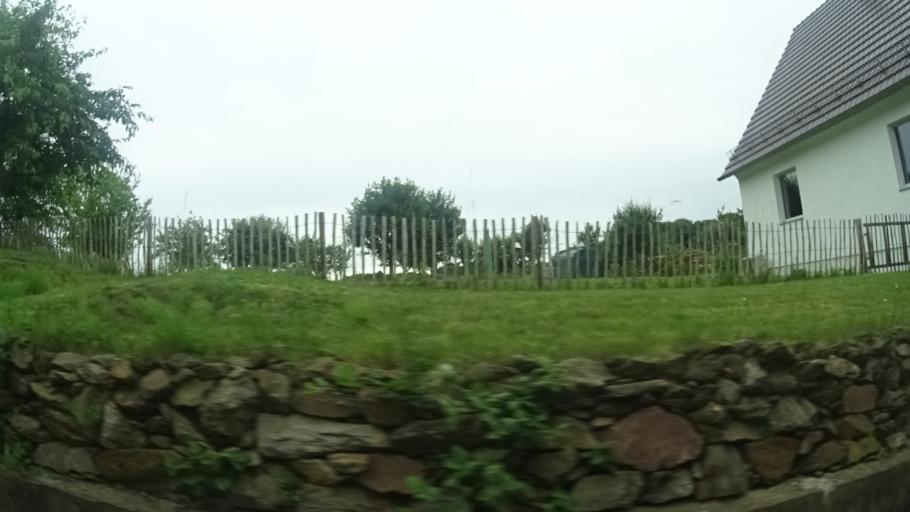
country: DE
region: Bavaria
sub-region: Regierungsbezirk Unterfranken
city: Mombris
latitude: 50.0871
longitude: 9.1864
